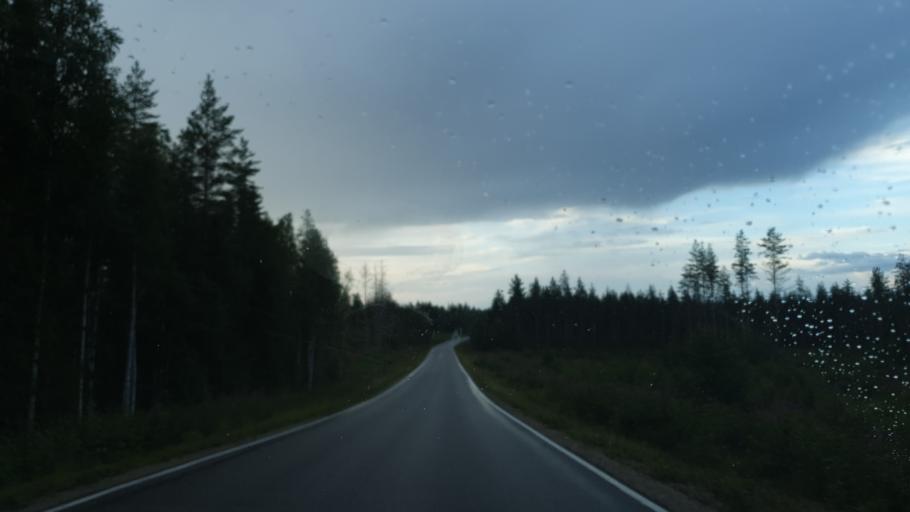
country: FI
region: North Karelia
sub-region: Pielisen Karjala
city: Lieksa
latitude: 63.6472
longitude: 29.8572
